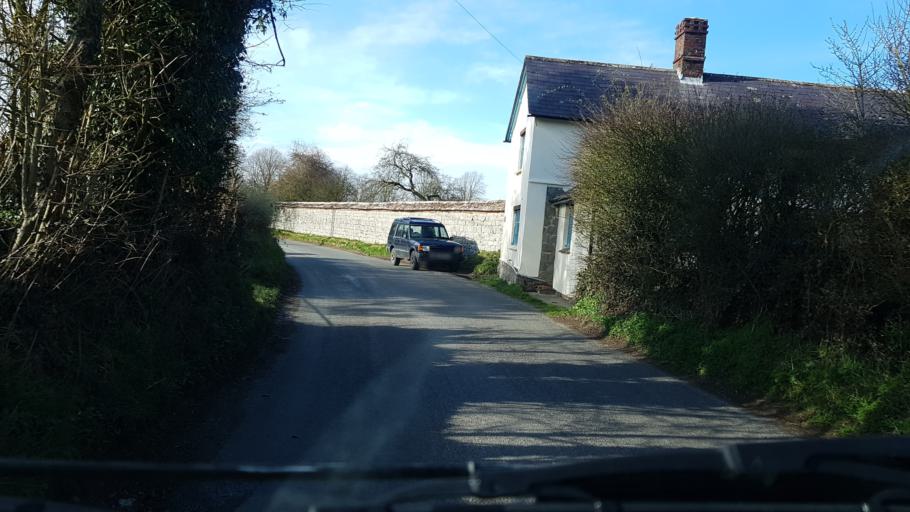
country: GB
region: England
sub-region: Wiltshire
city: Avebury
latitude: 51.4059
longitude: -1.8296
